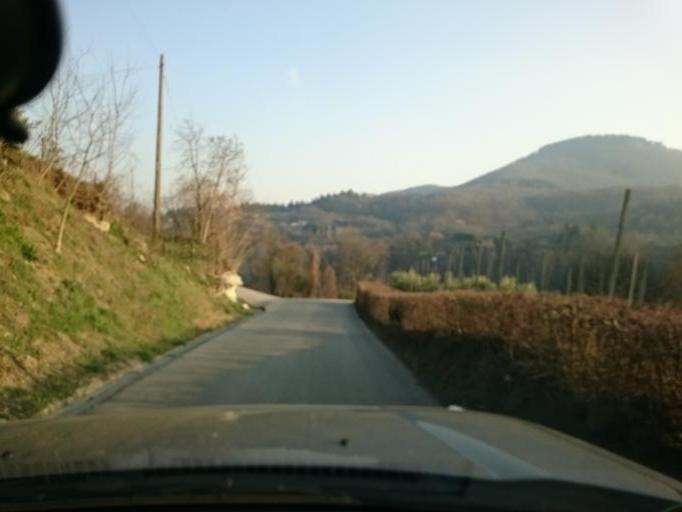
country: IT
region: Veneto
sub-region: Provincia di Padova
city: Torreglia
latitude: 45.3310
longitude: 11.7077
